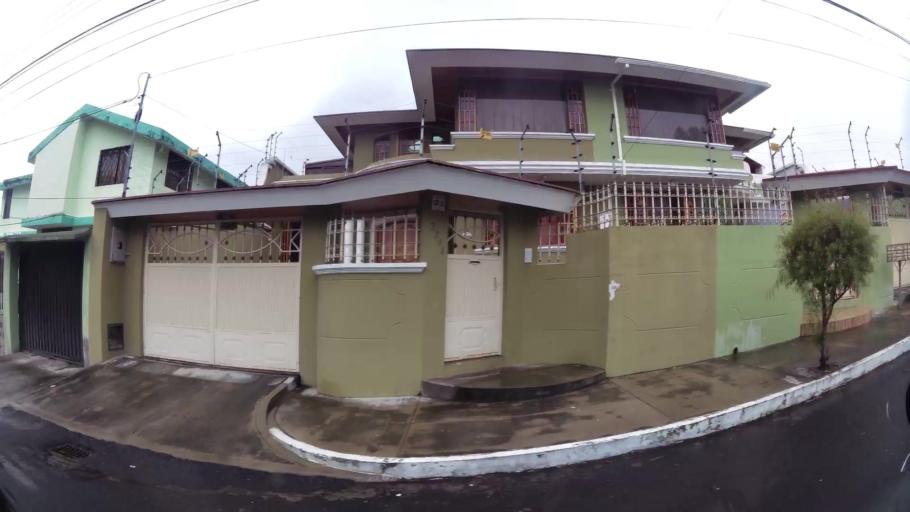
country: EC
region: Pichincha
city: Sangolqui
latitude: -0.3170
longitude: -78.4377
